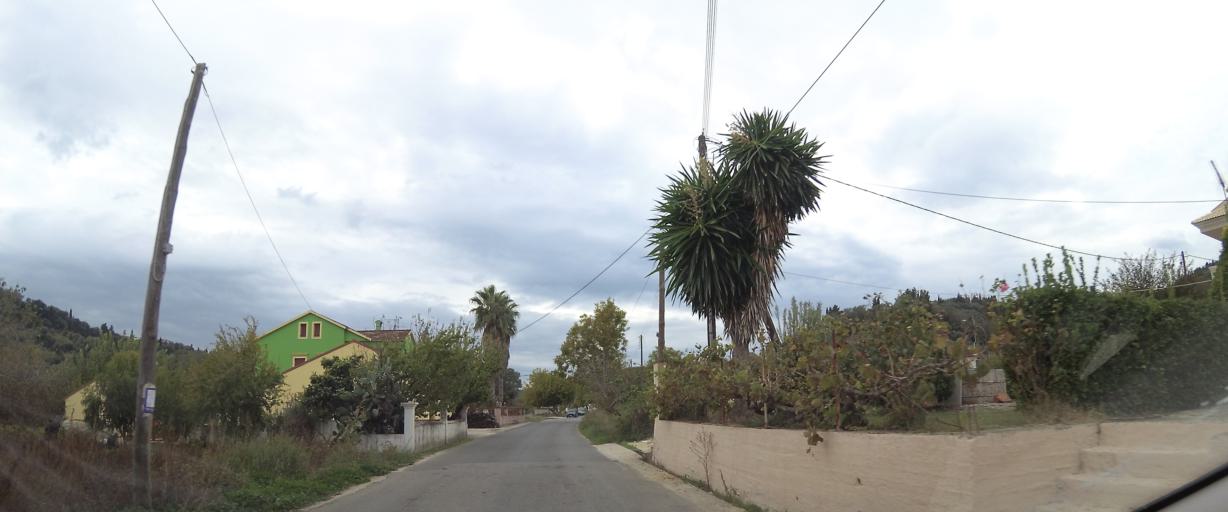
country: GR
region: Ionian Islands
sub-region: Nomos Kerkyras
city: Agios Georgis
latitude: 39.7644
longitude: 19.6944
